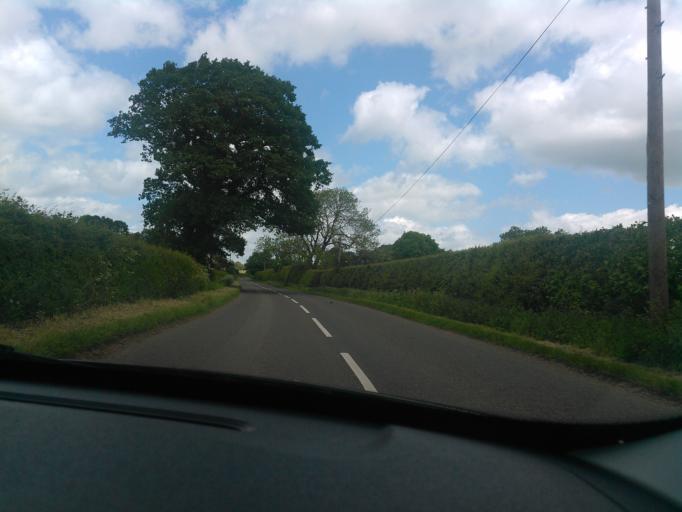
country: GB
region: England
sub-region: Shropshire
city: Prees
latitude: 52.8790
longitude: -2.6600
